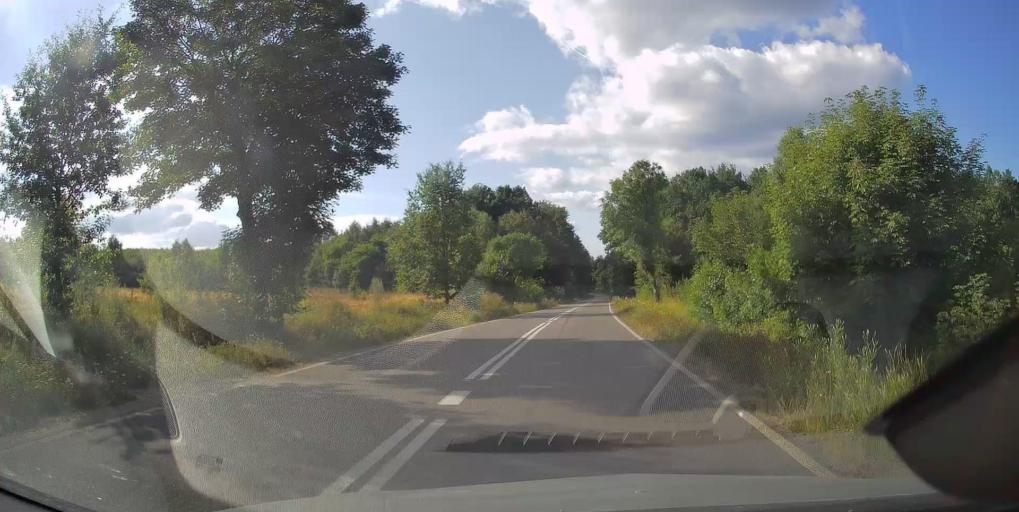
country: PL
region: Swietokrzyskie
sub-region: Powiat skarzyski
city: Suchedniow
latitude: 50.9898
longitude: 20.8631
